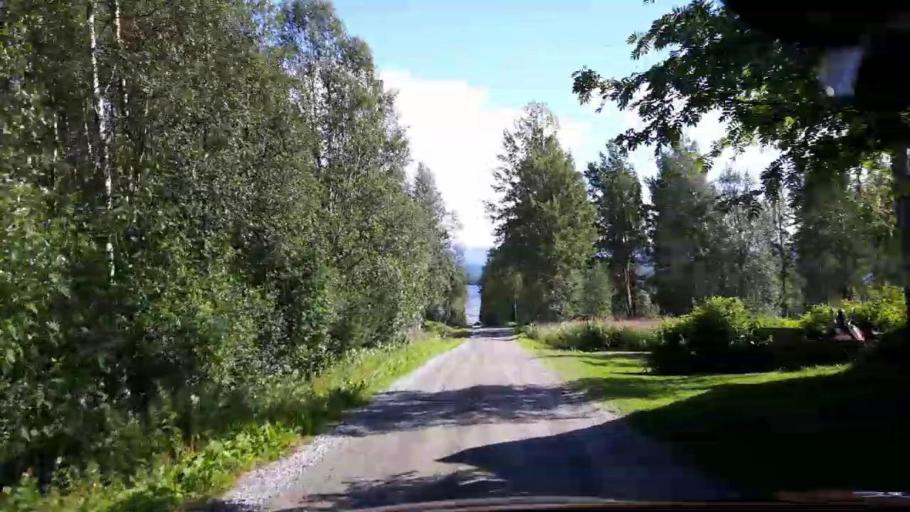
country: SE
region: Jaemtland
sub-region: Are Kommun
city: Are
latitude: 63.2115
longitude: 13.0538
